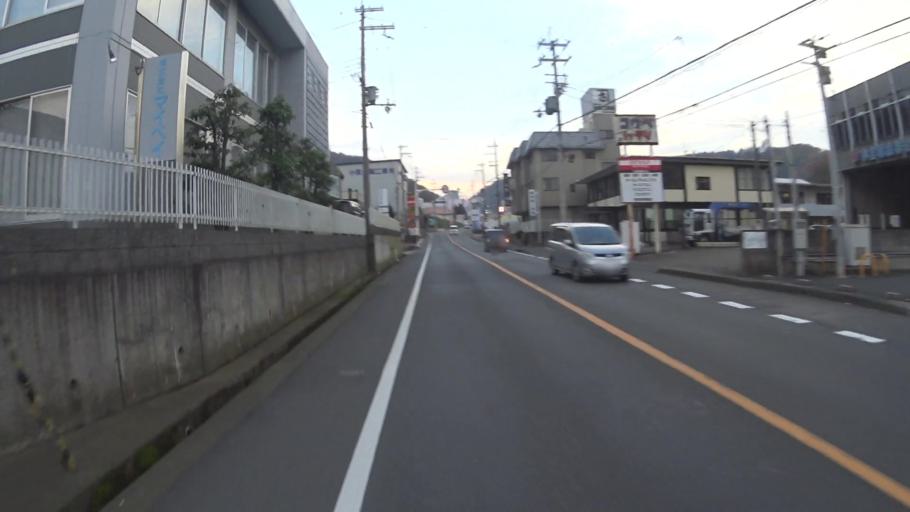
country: JP
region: Kyoto
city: Maizuru
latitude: 35.4600
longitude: 135.3823
